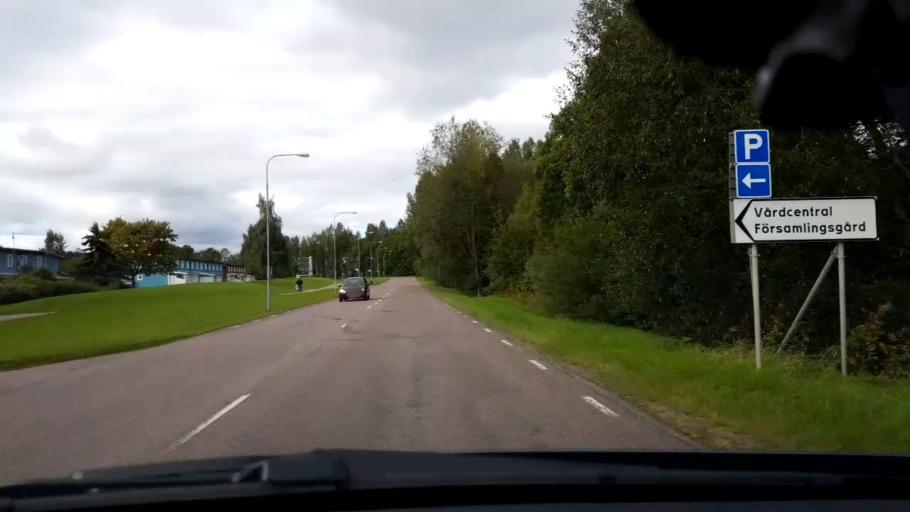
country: SE
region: Dalarna
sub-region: Borlange Kommun
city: Borlaenge
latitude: 60.4847
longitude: 15.4048
